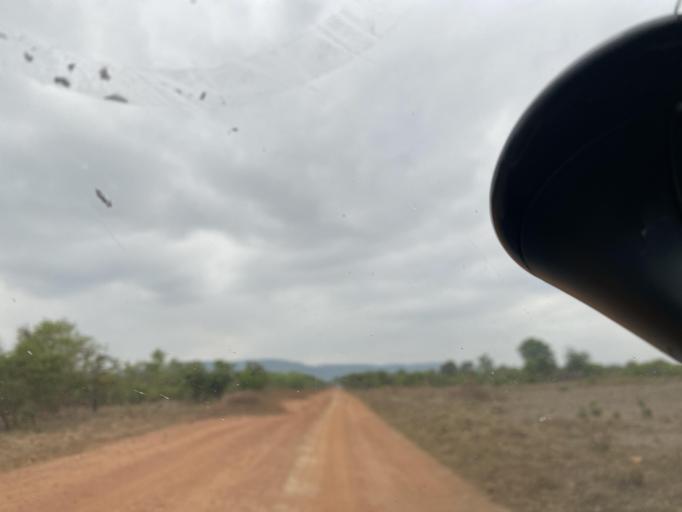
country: ZM
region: Lusaka
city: Chongwe
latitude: -15.2108
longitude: 28.7568
